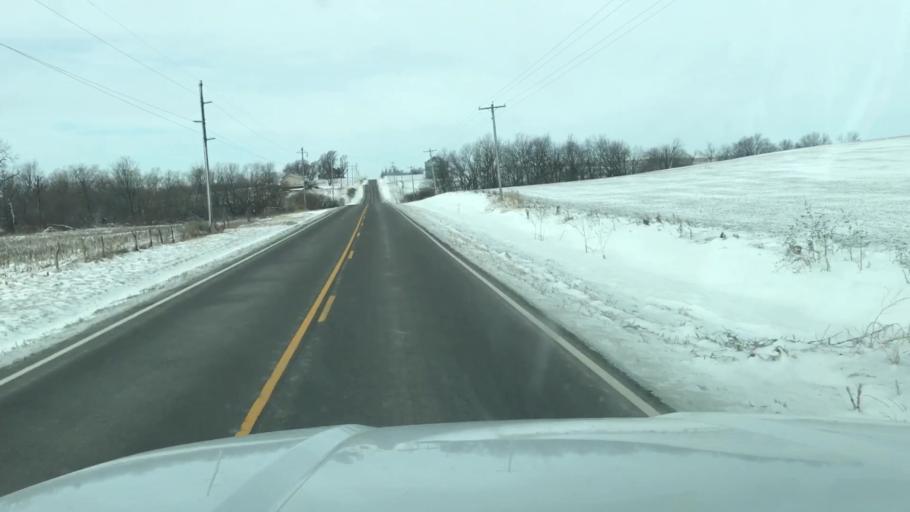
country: US
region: Missouri
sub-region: Holt County
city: Mound City
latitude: 40.1301
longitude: -95.1126
